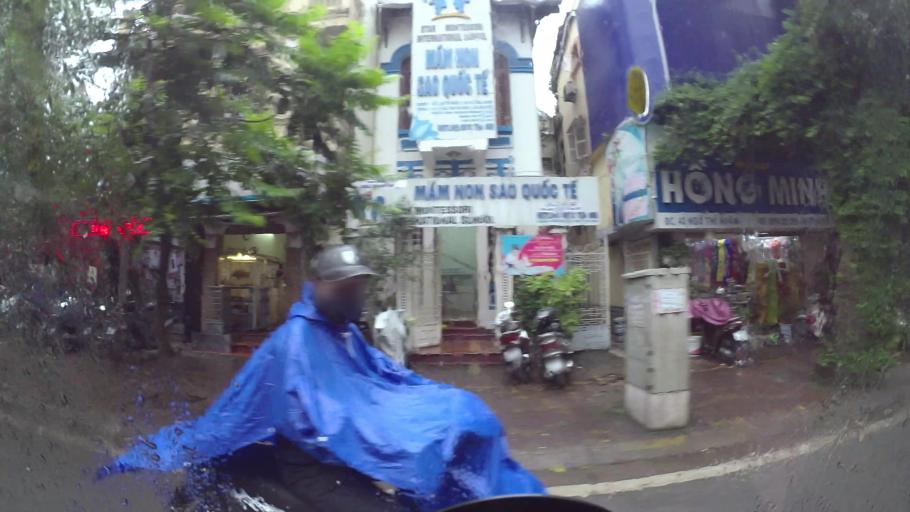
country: VN
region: Ha Noi
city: Hai BaTrung
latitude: 21.0163
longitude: 105.8530
